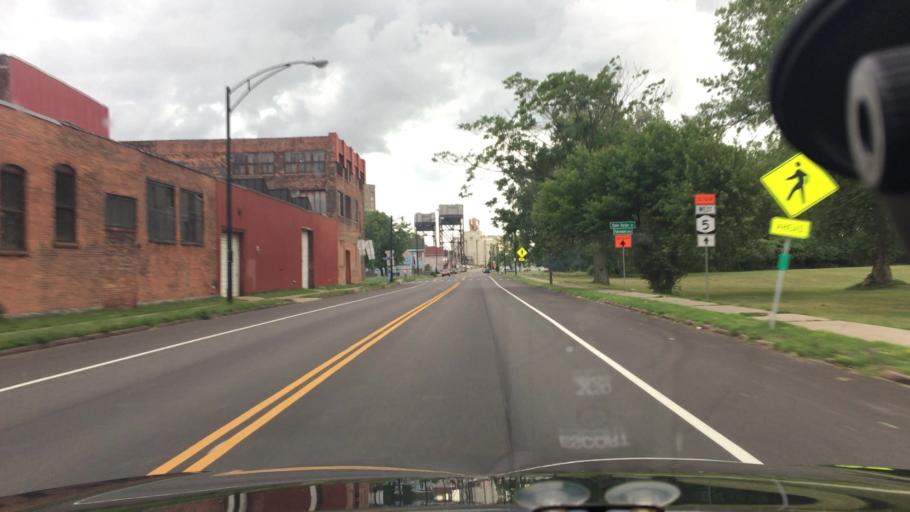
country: US
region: New York
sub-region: Erie County
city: Buffalo
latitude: 42.8678
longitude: -78.8659
